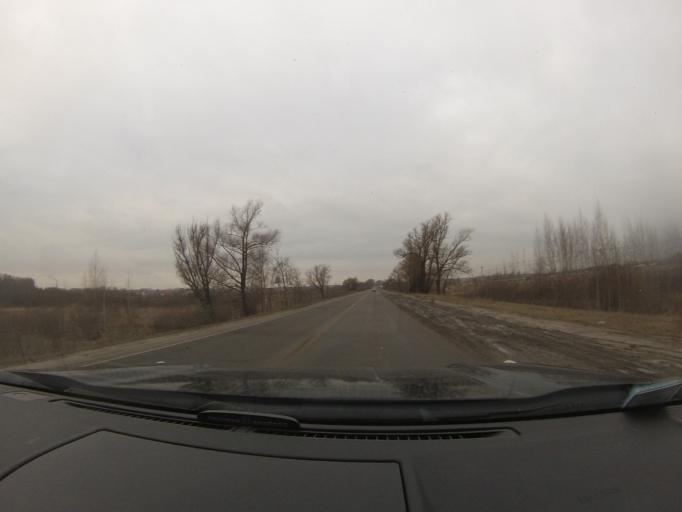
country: RU
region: Moskovskaya
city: Lopatinskiy
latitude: 55.3264
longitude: 38.7331
